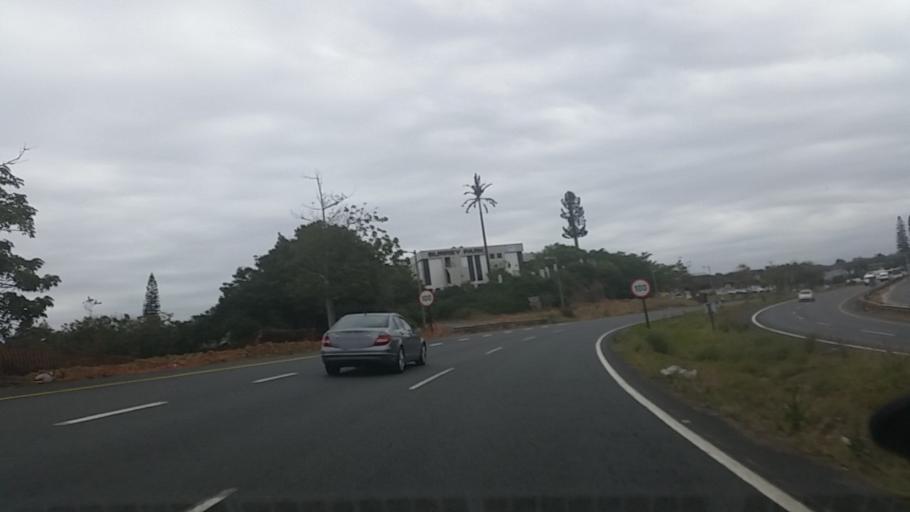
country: ZA
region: KwaZulu-Natal
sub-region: eThekwini Metropolitan Municipality
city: Berea
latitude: -29.8308
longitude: 30.9544
